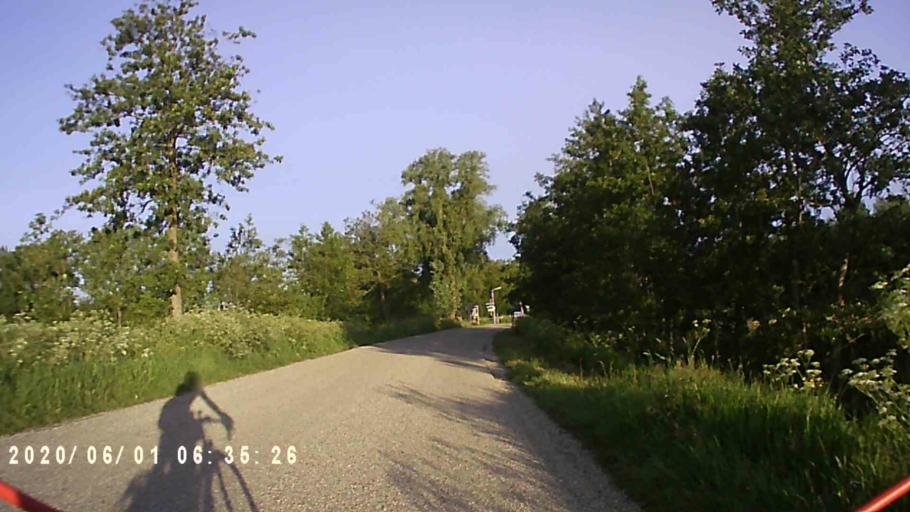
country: NL
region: Friesland
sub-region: Gemeente Kollumerland en Nieuwkruisland
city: Kollum
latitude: 53.2800
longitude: 6.1625
